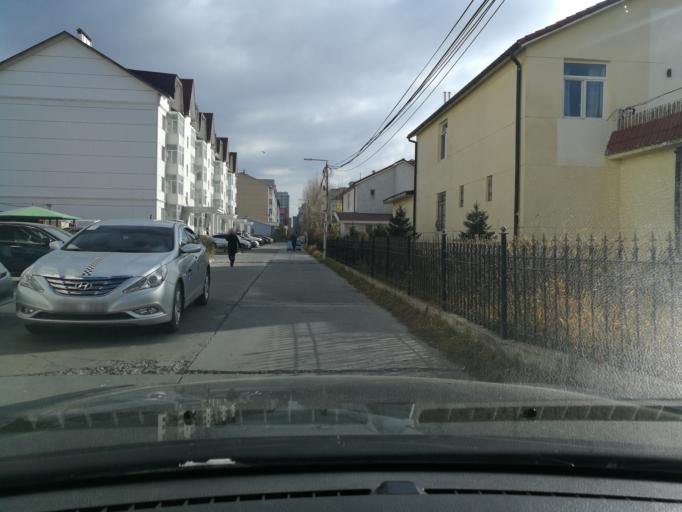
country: MN
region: Ulaanbaatar
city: Ulaanbaatar
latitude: 47.9055
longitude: 106.9219
